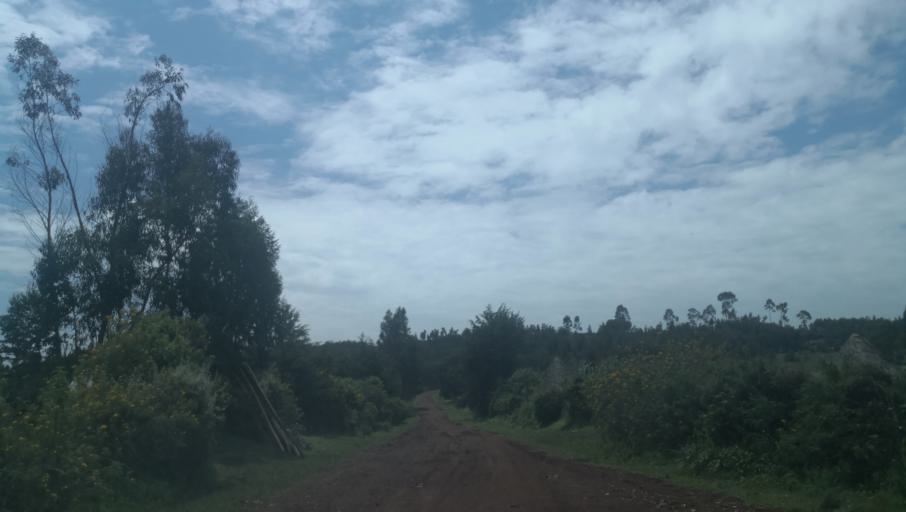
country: ET
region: Southern Nations, Nationalities, and People's Region
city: Butajira
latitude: 8.3003
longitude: 38.4730
